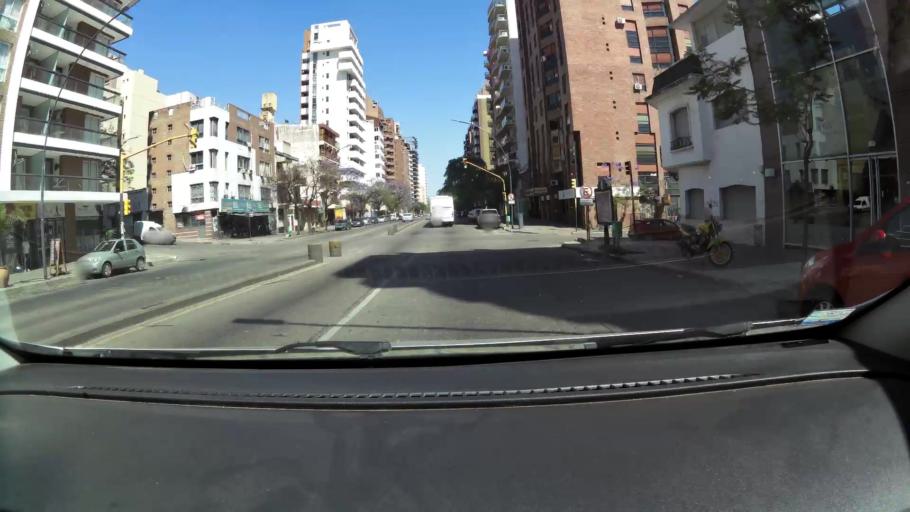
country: AR
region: Cordoba
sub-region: Departamento de Capital
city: Cordoba
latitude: -31.4184
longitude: -64.1952
